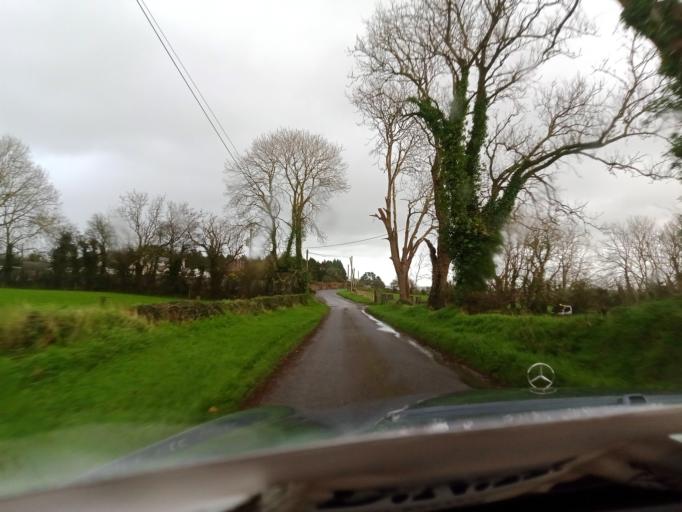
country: IE
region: Leinster
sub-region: Kilkenny
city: Mooncoin
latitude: 52.2678
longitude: -7.1890
